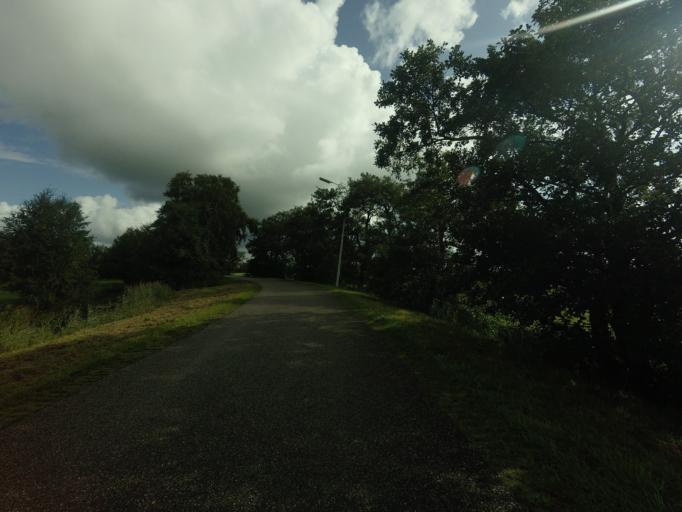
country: NL
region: Friesland
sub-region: Gemeente Tytsjerksteradiel
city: Garyp
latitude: 53.1521
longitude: 5.9489
